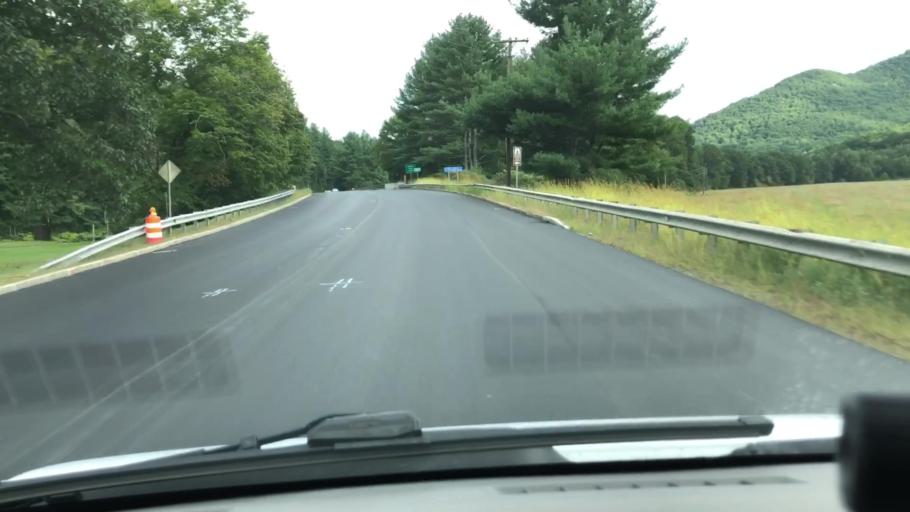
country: US
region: Massachusetts
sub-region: Franklin County
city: Charlemont
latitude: 42.6392
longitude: -72.9114
